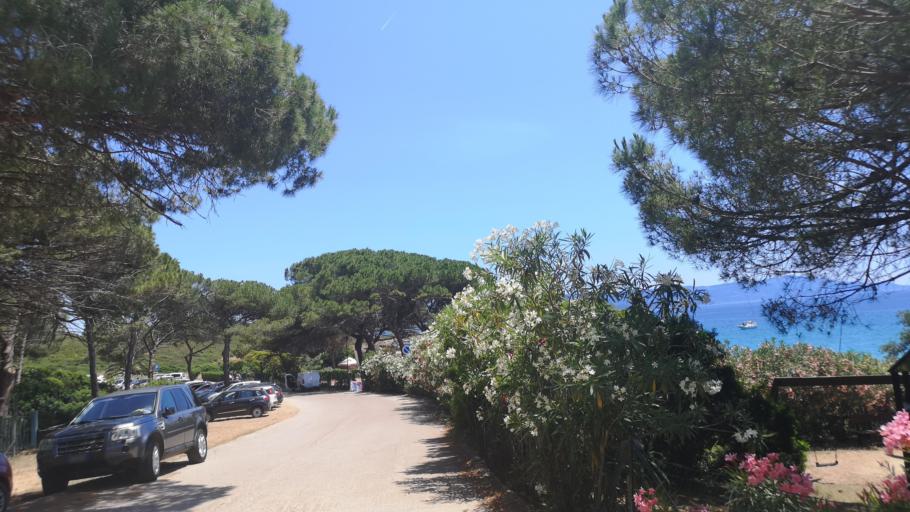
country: IT
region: Sardinia
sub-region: Provincia di Sassari
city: Alghero
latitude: 40.5851
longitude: 8.2576
